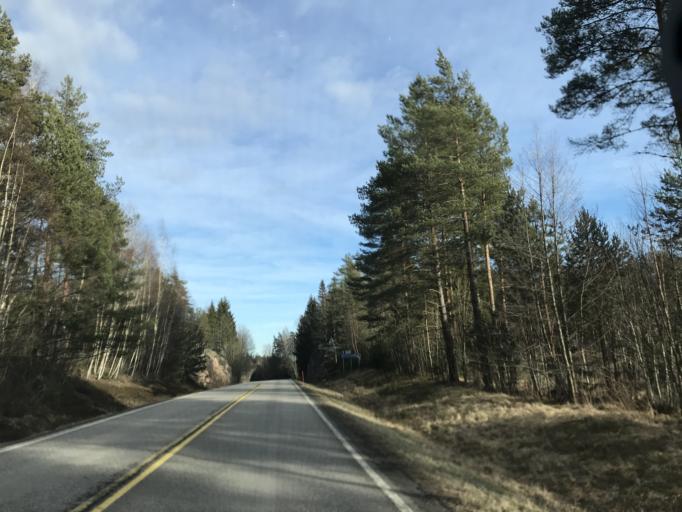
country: FI
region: Uusimaa
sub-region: Raaseporin
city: Ekenaes
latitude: 60.0828
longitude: 23.3980
